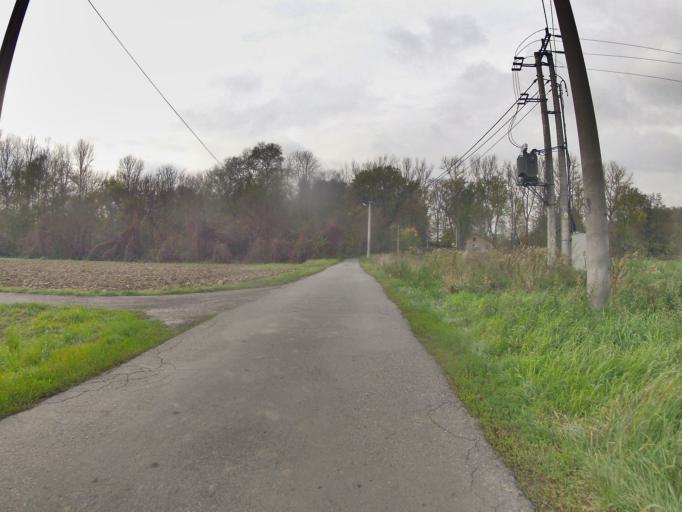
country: PL
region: Lesser Poland Voivodeship
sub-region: Powiat wielicki
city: Wegrzce Wielkie
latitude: 50.0464
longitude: 20.1015
